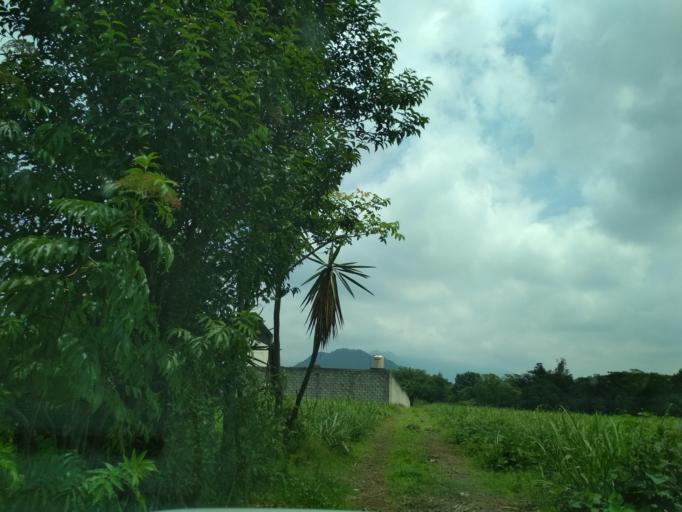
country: MX
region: Veracruz
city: Atzacan
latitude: 18.8803
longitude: -97.0773
